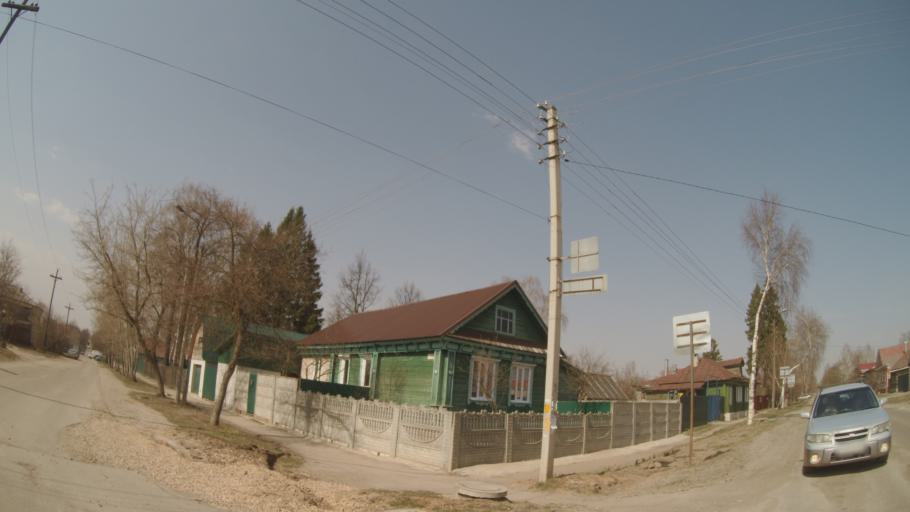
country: RU
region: Nizjnij Novgorod
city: Arzamas
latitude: 55.3889
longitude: 43.8248
